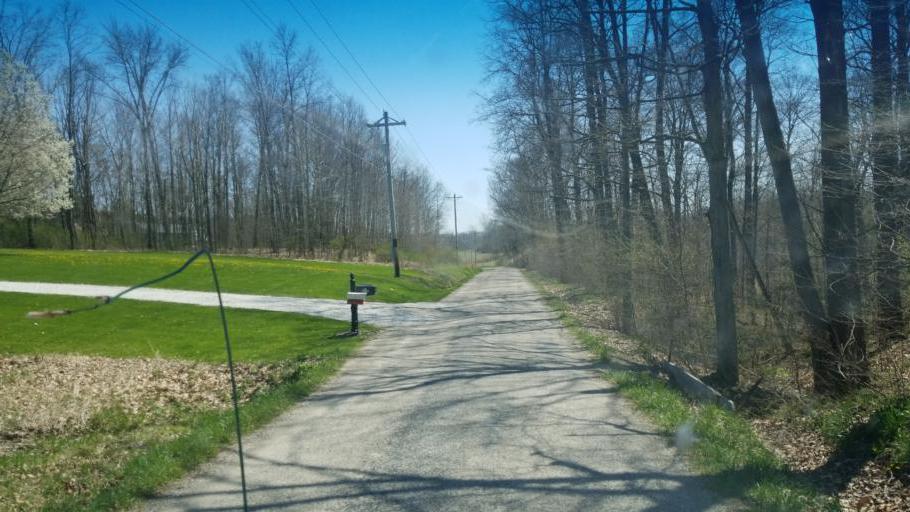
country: US
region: Ohio
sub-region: Ashland County
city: Ashland
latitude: 40.8455
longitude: -82.3877
